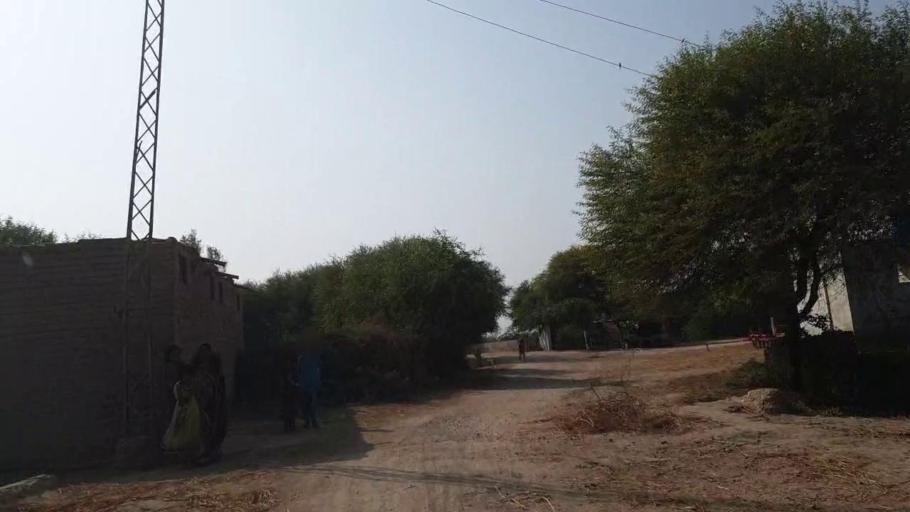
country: PK
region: Sindh
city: Kario
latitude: 24.9407
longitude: 68.5380
